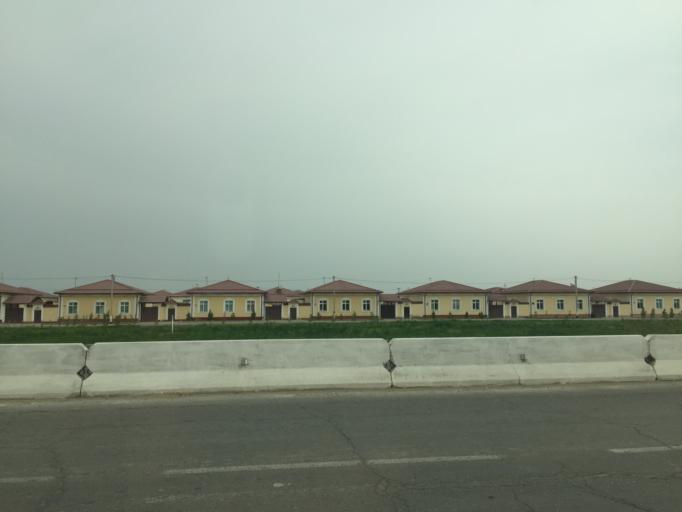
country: UZ
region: Bukhara
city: Kogon
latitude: 39.7344
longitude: 64.5087
